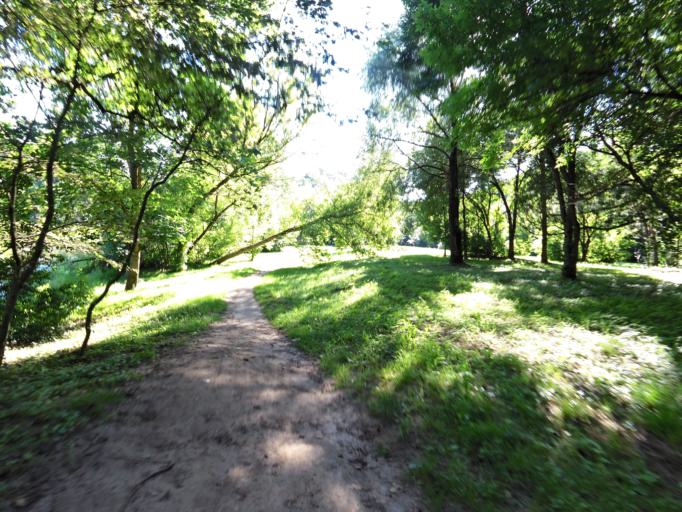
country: LT
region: Vilnius County
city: Vilkpede
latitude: 54.6906
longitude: 25.2327
